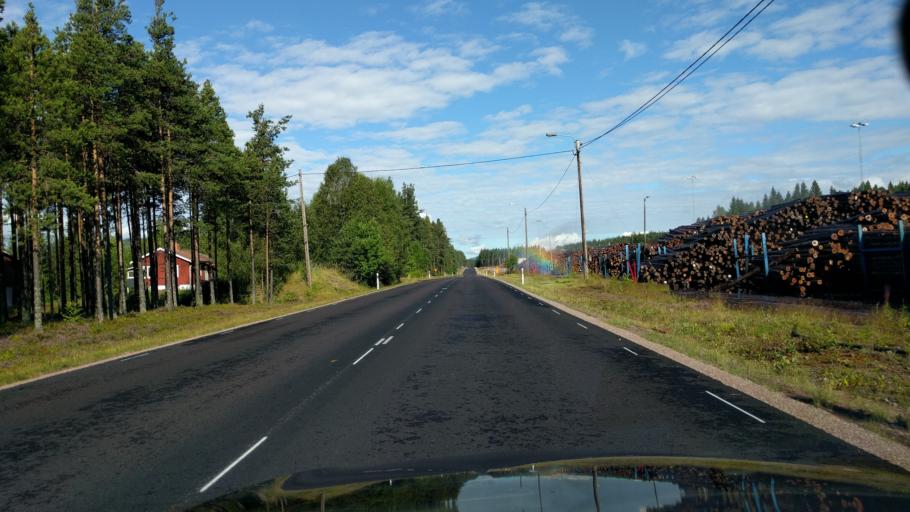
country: SE
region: Dalarna
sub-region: Alvdalens Kommun
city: AElvdalen
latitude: 61.1523
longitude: 14.1368
